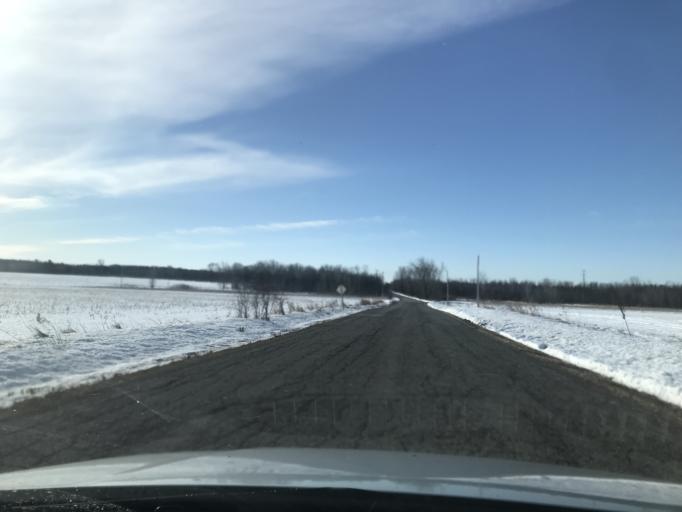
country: US
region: Wisconsin
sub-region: Oconto County
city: Oconto Falls
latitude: 44.9382
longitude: -88.0167
